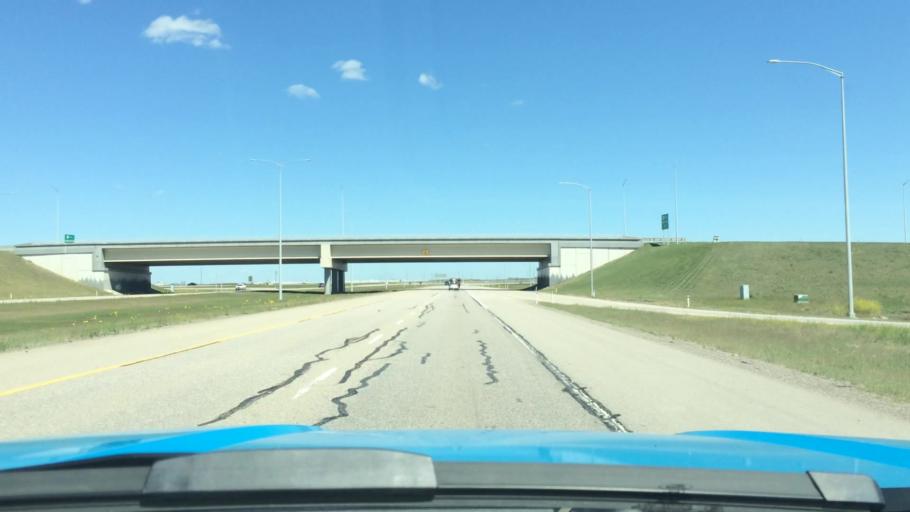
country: CA
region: Alberta
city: Chestermere
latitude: 51.1528
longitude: -113.9210
